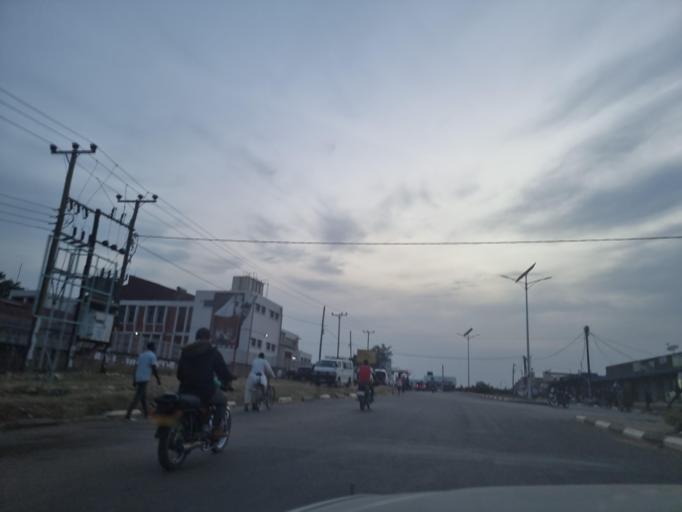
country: UG
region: Northern Region
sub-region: Arua District
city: Arua
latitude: 3.0211
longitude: 30.9124
